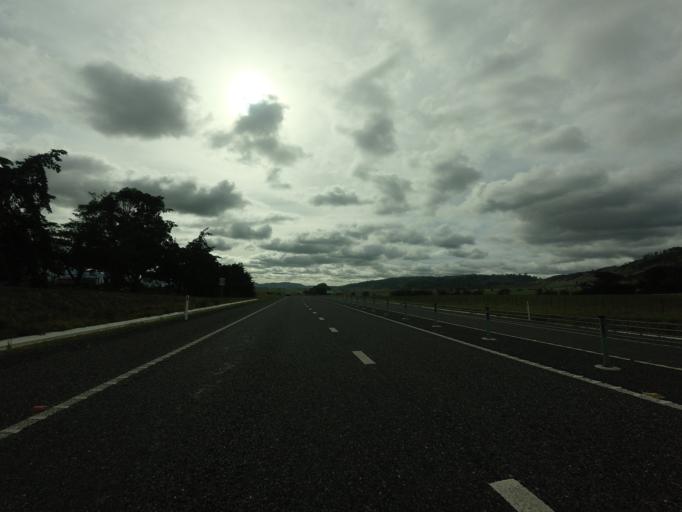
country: AU
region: Tasmania
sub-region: Brighton
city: Bridgewater
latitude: -42.5394
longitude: 147.2063
